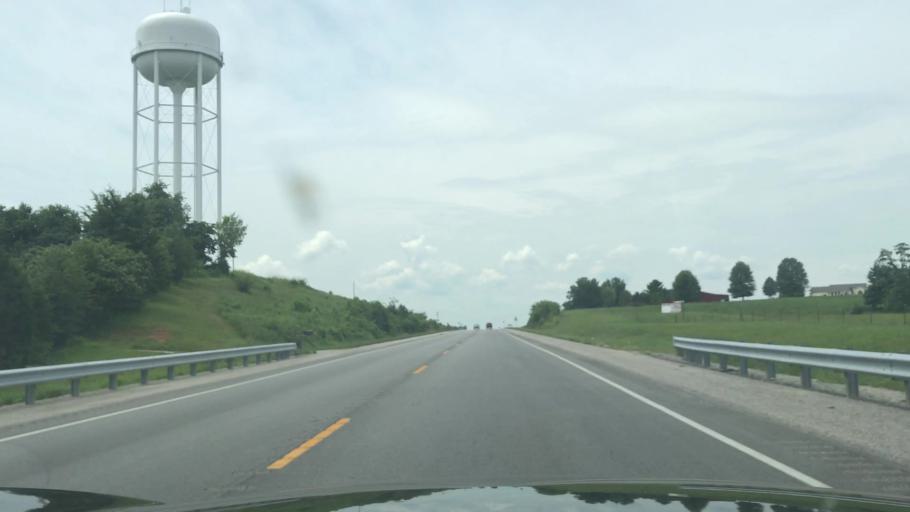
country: US
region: Kentucky
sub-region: Green County
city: Greensburg
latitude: 37.3085
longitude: -85.4328
